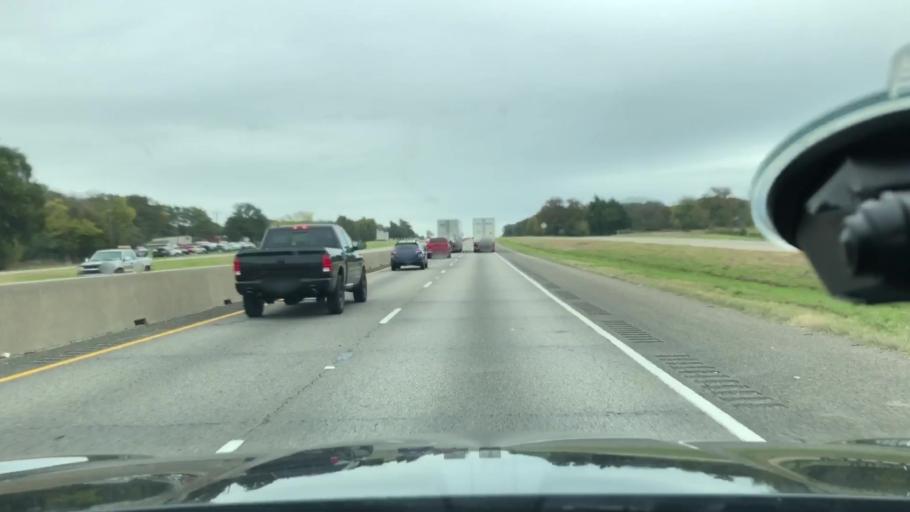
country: US
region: Texas
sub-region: Hopkins County
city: Sulphur Springs
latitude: 33.1464
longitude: -95.5490
